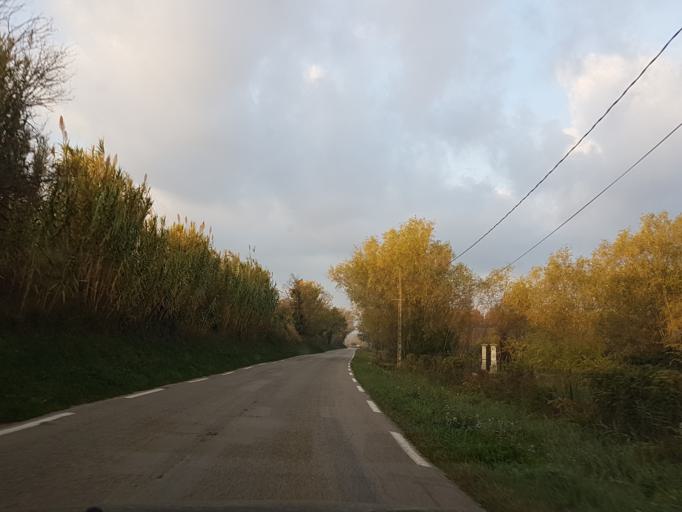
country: FR
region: Provence-Alpes-Cote d'Azur
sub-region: Departement du Vaucluse
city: Althen-des-Paluds
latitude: 44.0370
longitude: 4.9572
